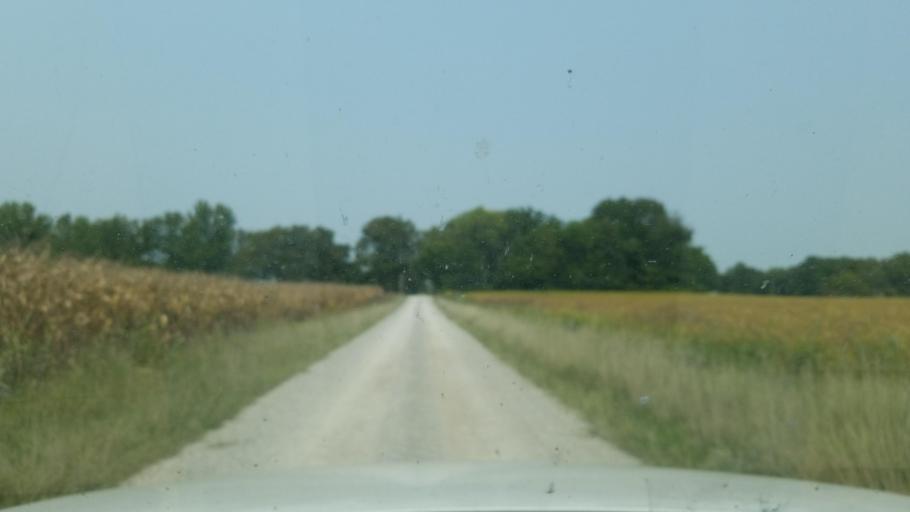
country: US
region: Illinois
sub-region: Saline County
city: Eldorado
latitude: 37.8220
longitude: -88.5167
